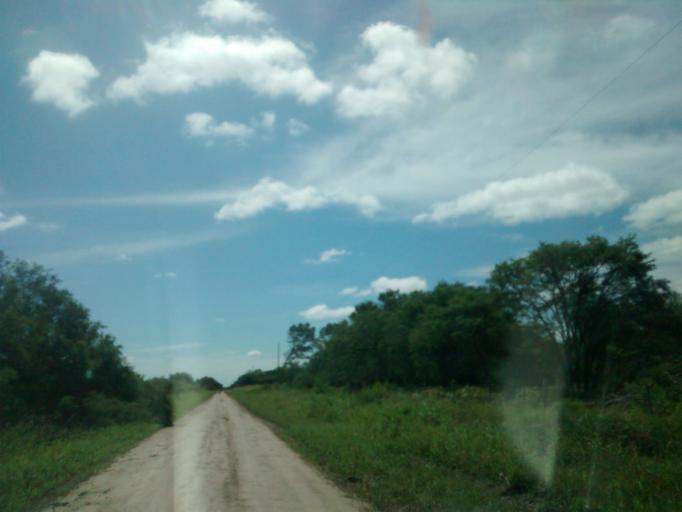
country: AR
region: Chaco
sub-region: Departamento de Quitilipi
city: Quitilipi
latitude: -26.7844
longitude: -60.2205
